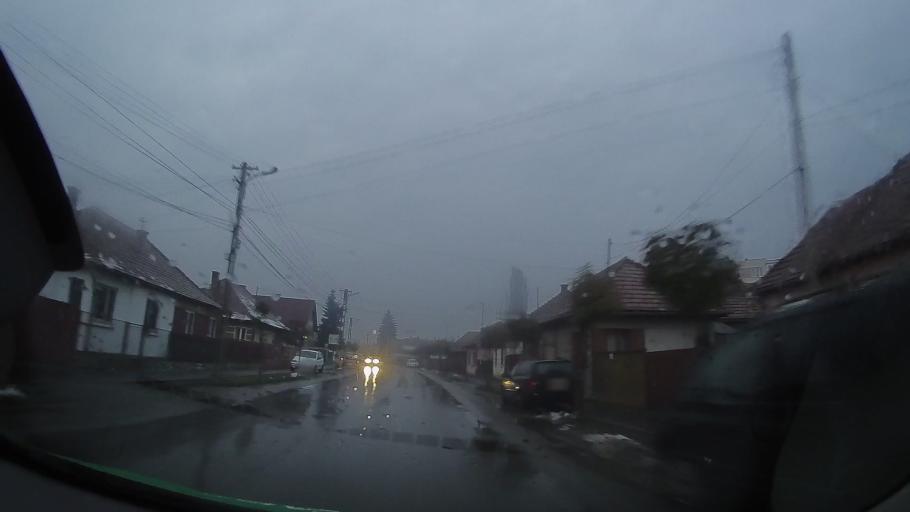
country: RO
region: Harghita
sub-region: Municipiul Gheorgheni
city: Gheorgheni
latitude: 46.7223
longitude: 25.5899
